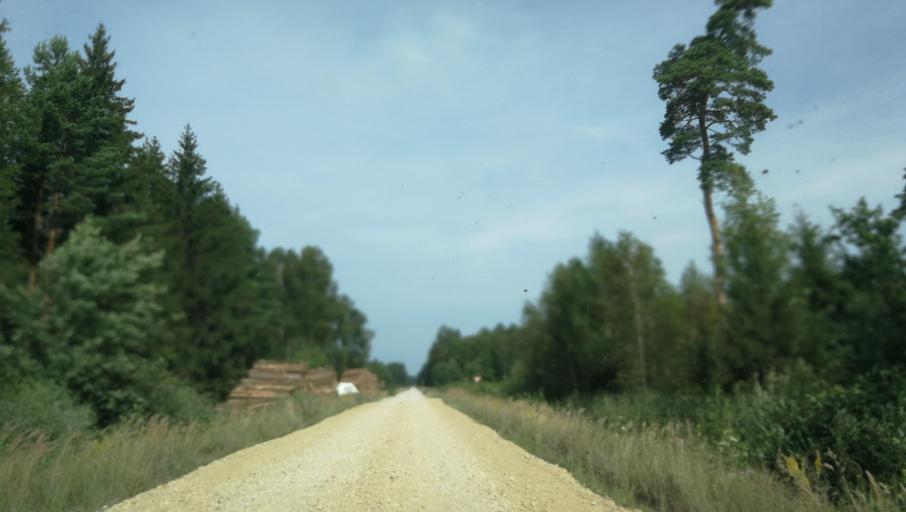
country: LV
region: Durbe
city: Liegi
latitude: 56.7624
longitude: 21.3556
